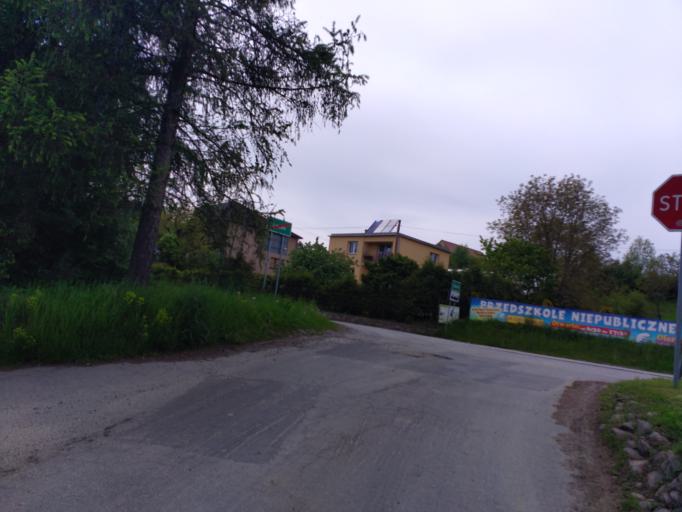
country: PL
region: Lesser Poland Voivodeship
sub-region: Powiat nowosadecki
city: Lacko
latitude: 49.5536
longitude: 20.4276
